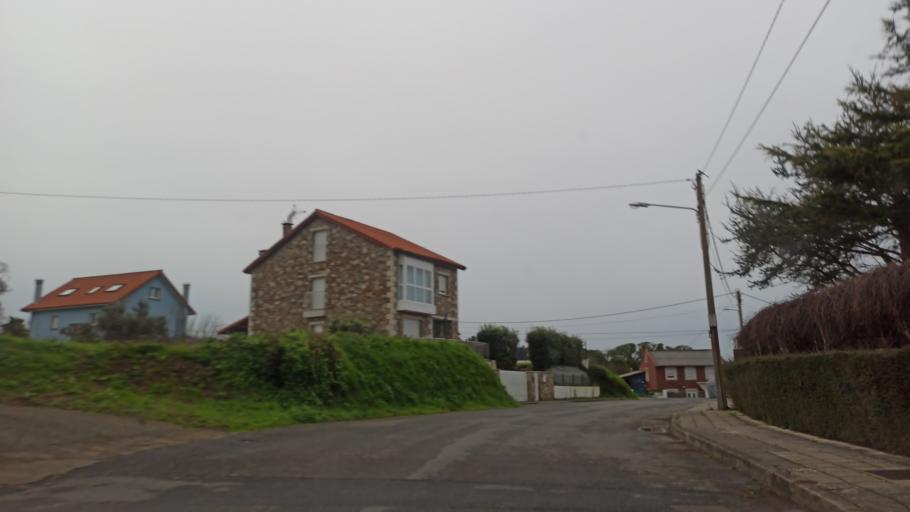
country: ES
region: Galicia
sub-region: Provincia da Coruna
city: Oleiros
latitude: 43.3948
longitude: -8.3255
